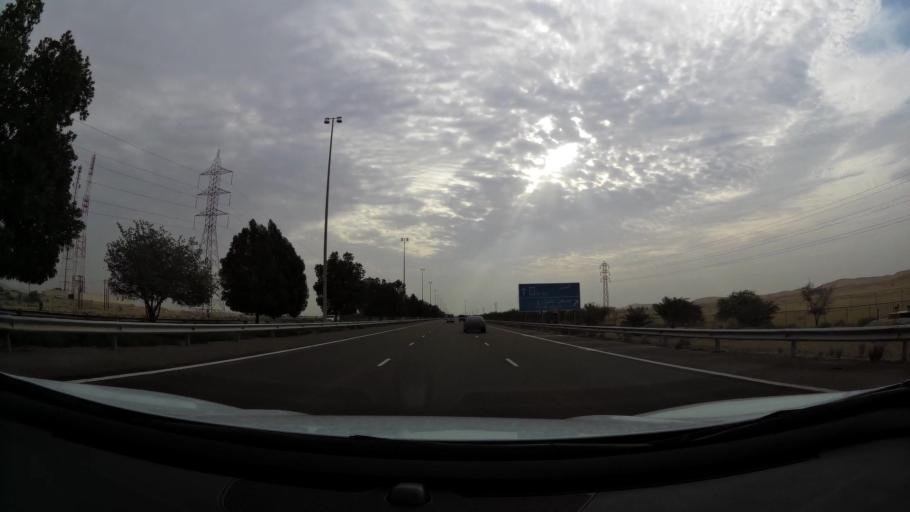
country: AE
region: Abu Dhabi
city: Abu Dhabi
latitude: 24.1951
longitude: 54.9351
